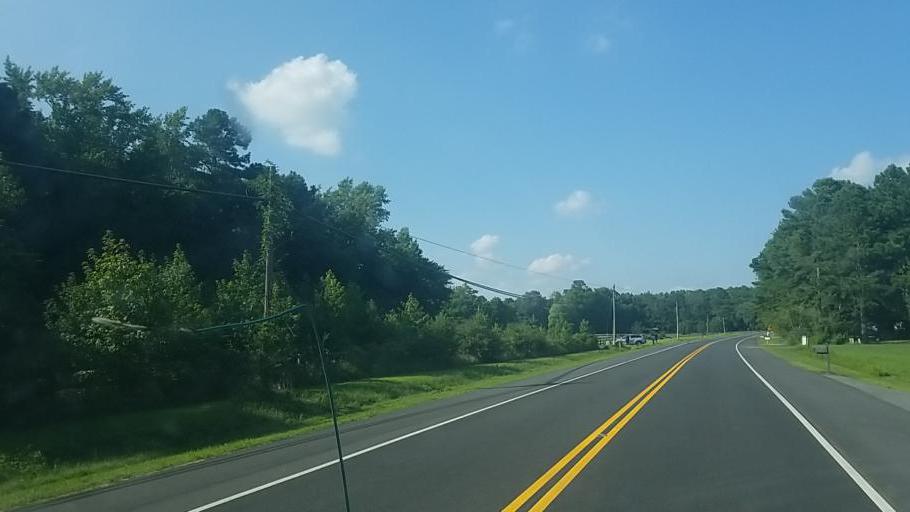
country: US
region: Maryland
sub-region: Worcester County
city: Berlin
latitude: 38.3672
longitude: -75.2003
